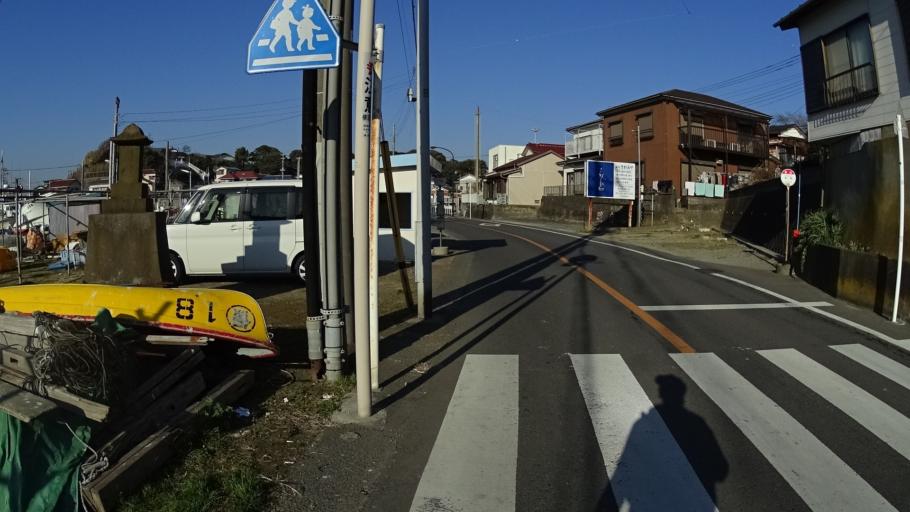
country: JP
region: Kanagawa
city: Miura
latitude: 35.1999
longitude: 139.6065
